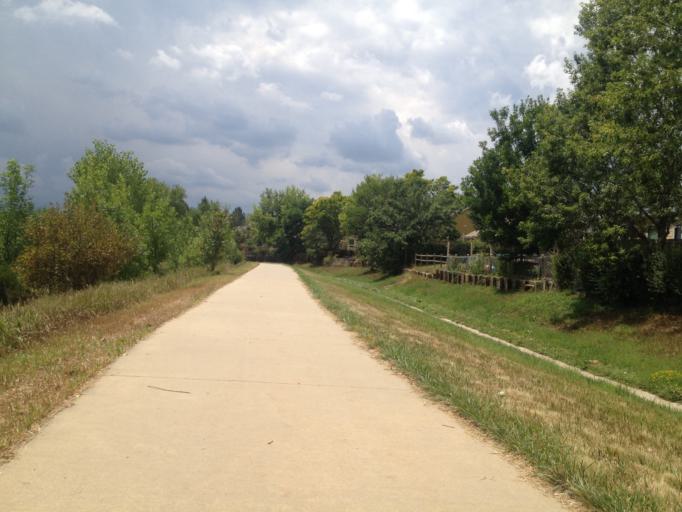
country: US
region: Colorado
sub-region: Boulder County
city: Louisville
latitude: 39.9688
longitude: -105.1481
